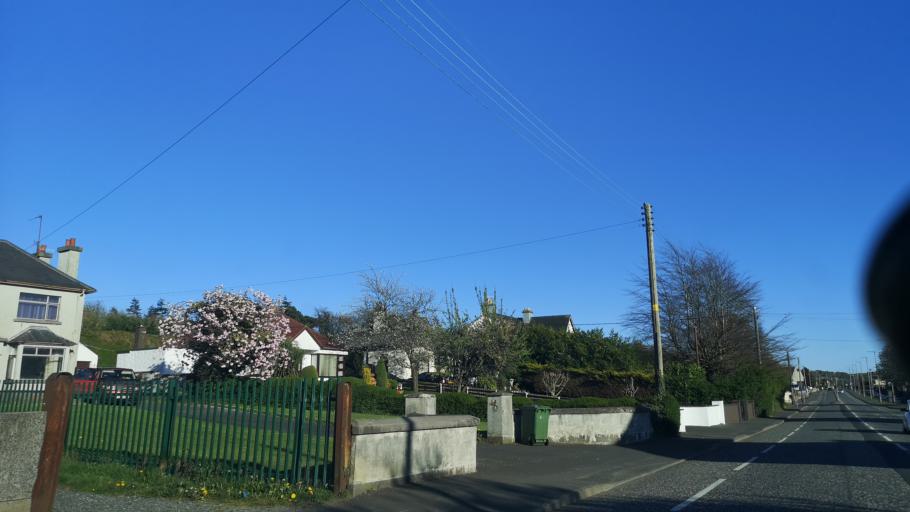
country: GB
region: Northern Ireland
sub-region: Newry and Mourne District
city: Newry
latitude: 54.1877
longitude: -6.3468
